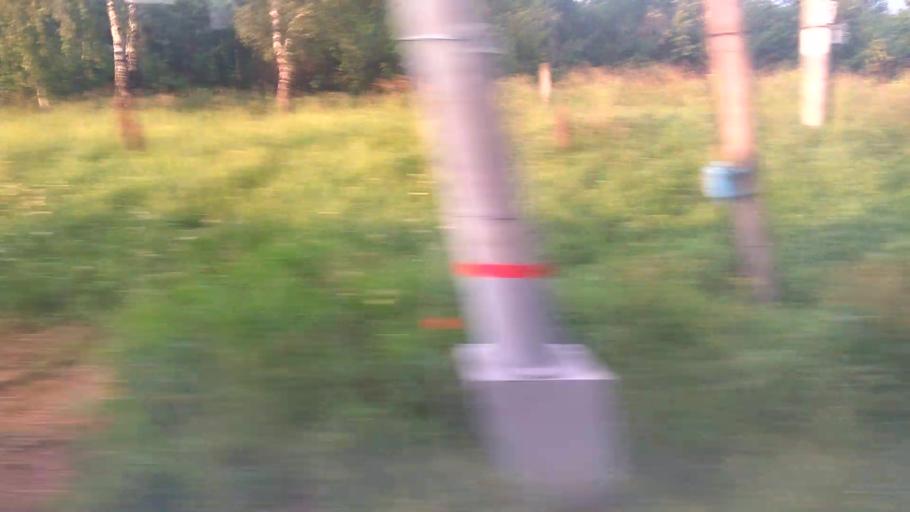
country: RU
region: Moskovskaya
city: Stupino
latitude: 54.8845
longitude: 38.1003
